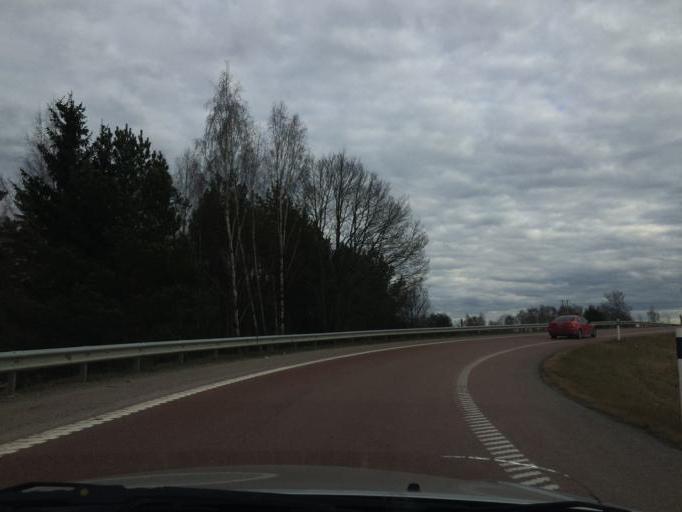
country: SE
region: Soedermanland
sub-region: Eskilstuna Kommun
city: Torshalla
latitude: 59.3937
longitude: 16.4697
